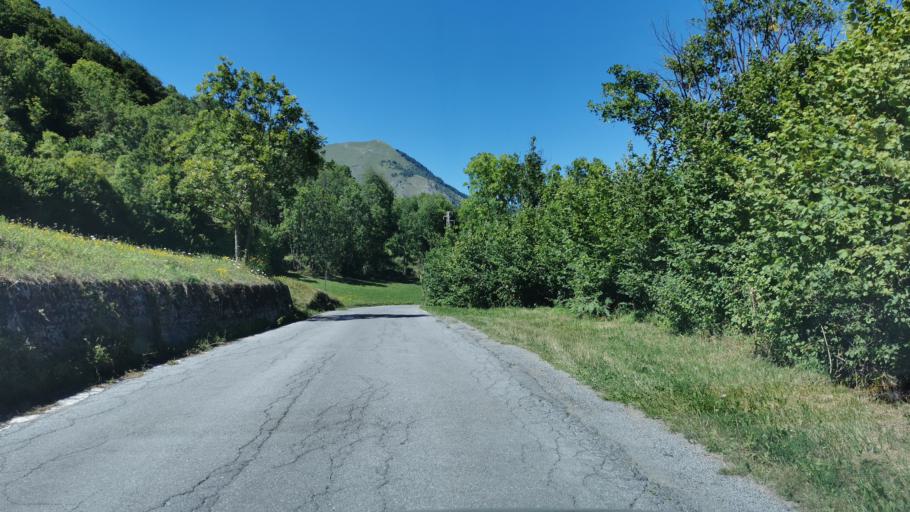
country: IT
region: Piedmont
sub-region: Provincia di Cuneo
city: Entracque
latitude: 44.2394
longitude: 7.3908
